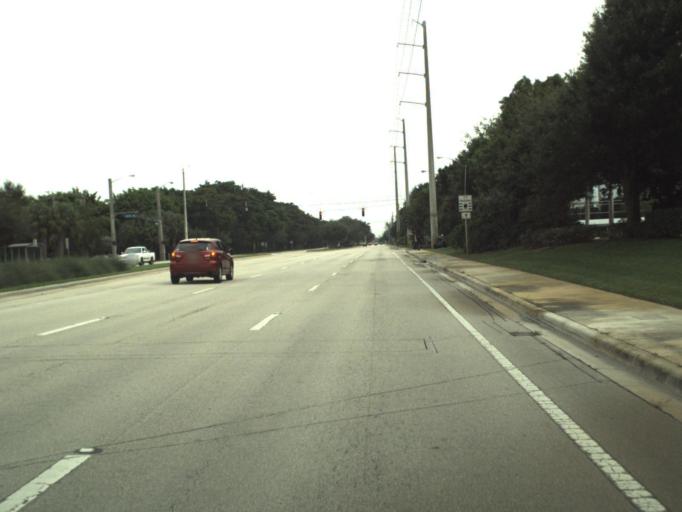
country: US
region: Florida
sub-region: Palm Beach County
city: Boca Del Mar
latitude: 26.3711
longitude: -80.1210
